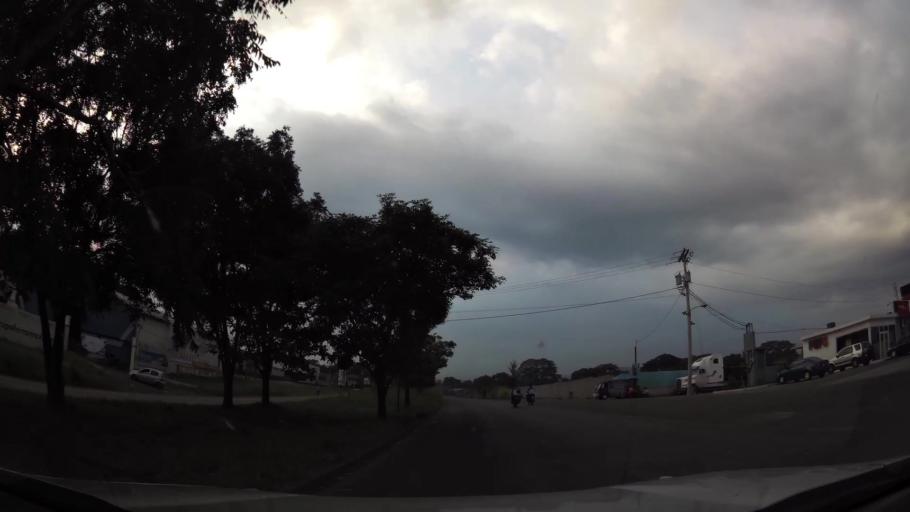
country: GT
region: Escuintla
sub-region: Municipio de Escuintla
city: Escuintla
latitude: 14.2808
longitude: -90.7826
